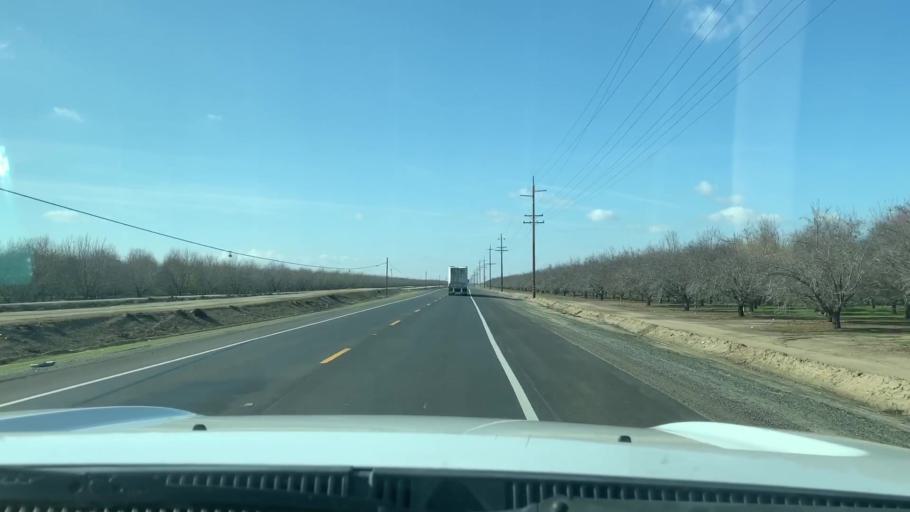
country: US
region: California
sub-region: Kern County
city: Wasco
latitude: 35.6018
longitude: -119.2805
